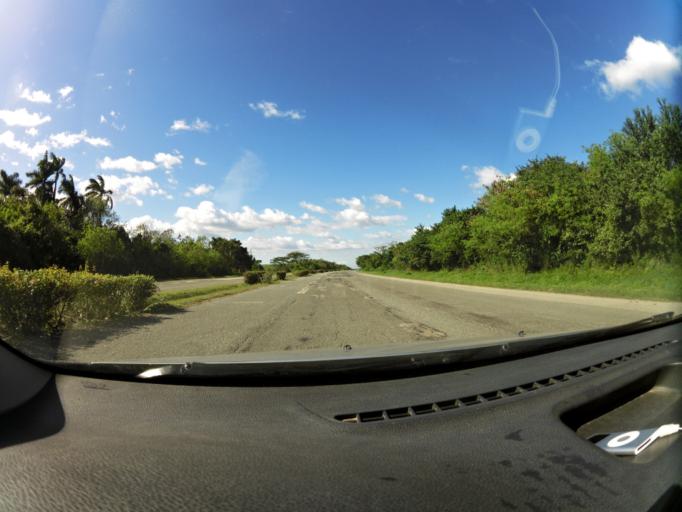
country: CU
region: Santiago de Cuba
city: San Luis
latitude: 20.1426
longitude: -75.7717
